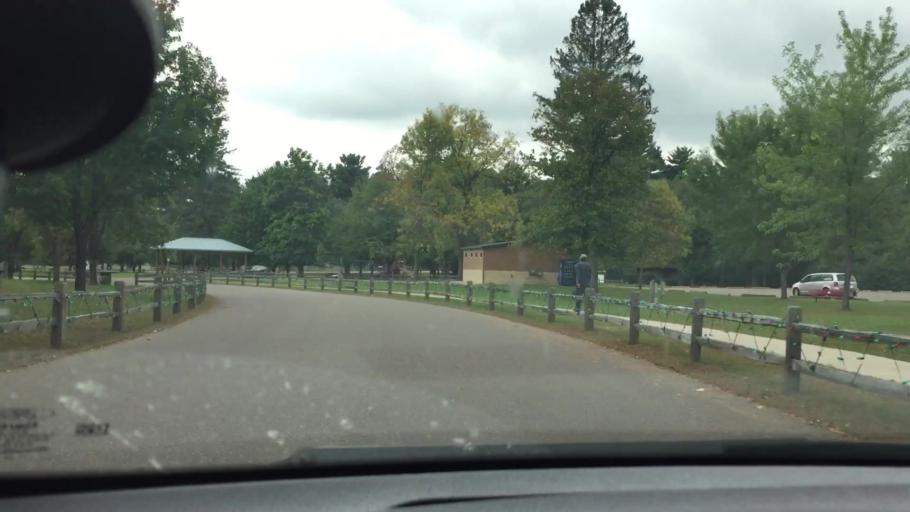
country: US
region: Wisconsin
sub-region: Chippewa County
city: Chippewa Falls
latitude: 44.9460
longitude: -91.4003
